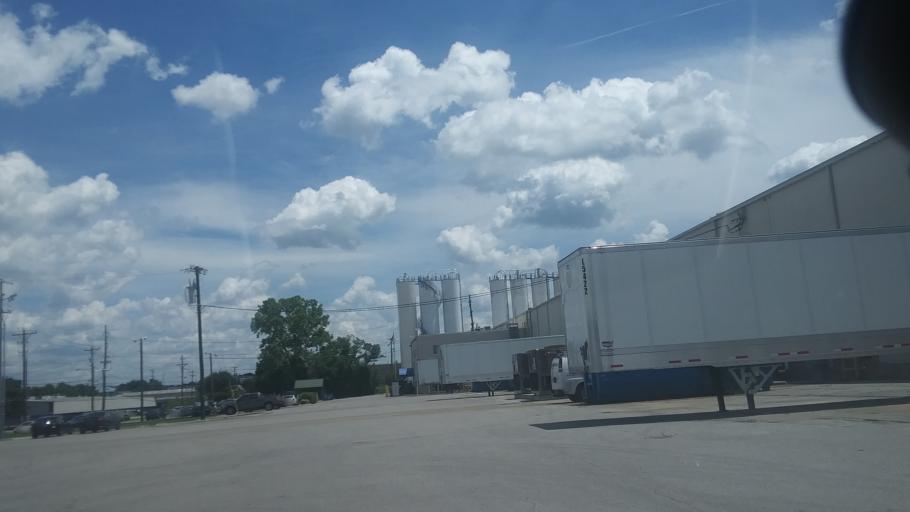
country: US
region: Tennessee
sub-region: Davidson County
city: Oak Hill
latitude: 36.0924
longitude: -86.6931
